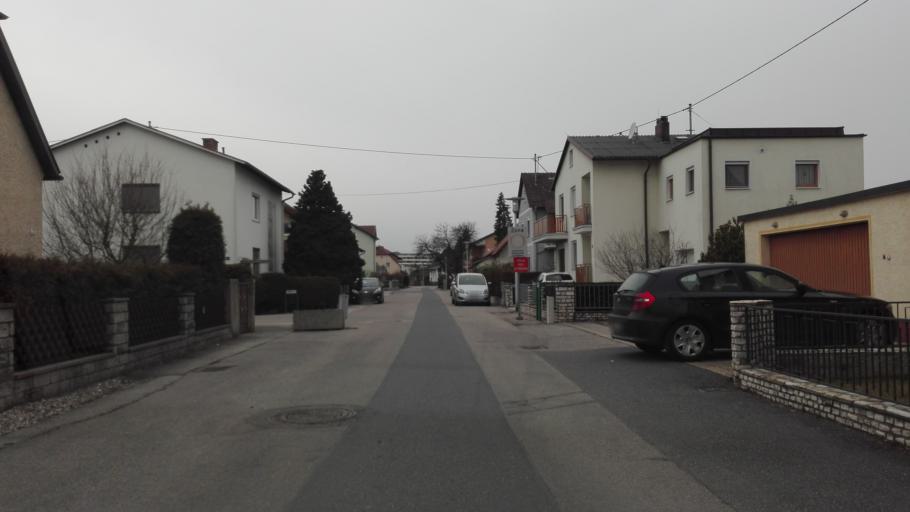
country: AT
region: Upper Austria
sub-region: Politischer Bezirk Linz-Land
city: Traun
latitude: 48.2454
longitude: 14.2452
